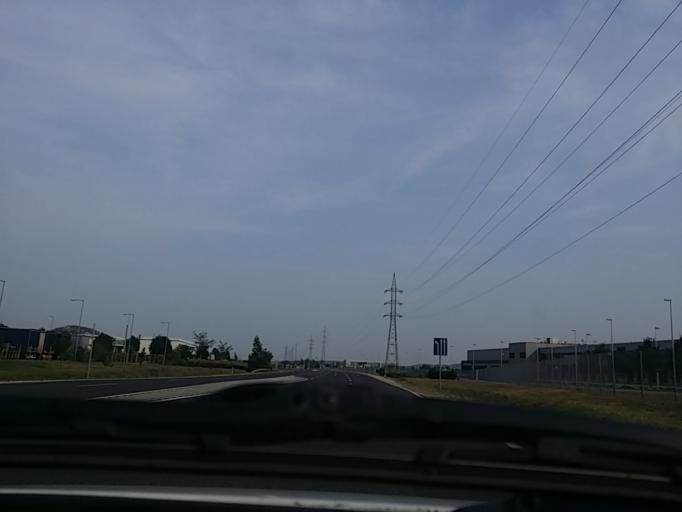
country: HU
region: Pest
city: Biatorbagy
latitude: 47.4700
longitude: 18.8709
